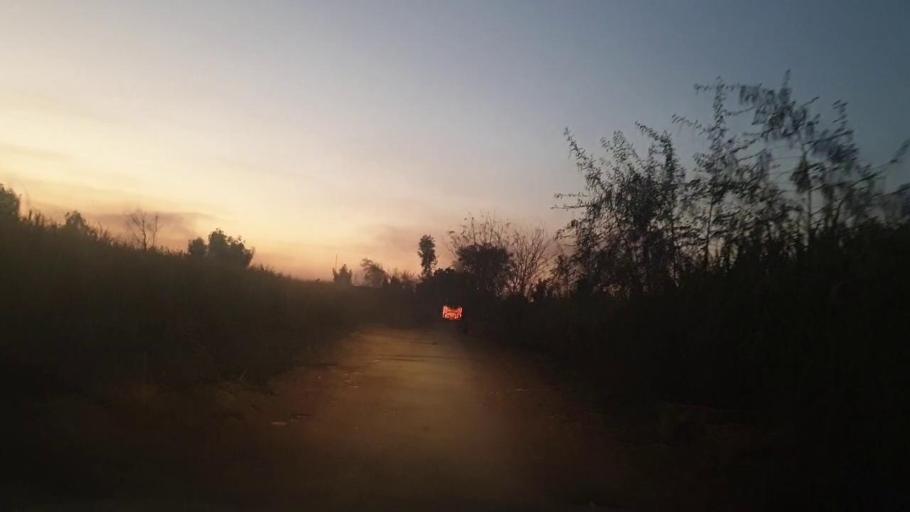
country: PK
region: Sindh
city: Ghotki
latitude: 28.0308
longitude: 69.3605
